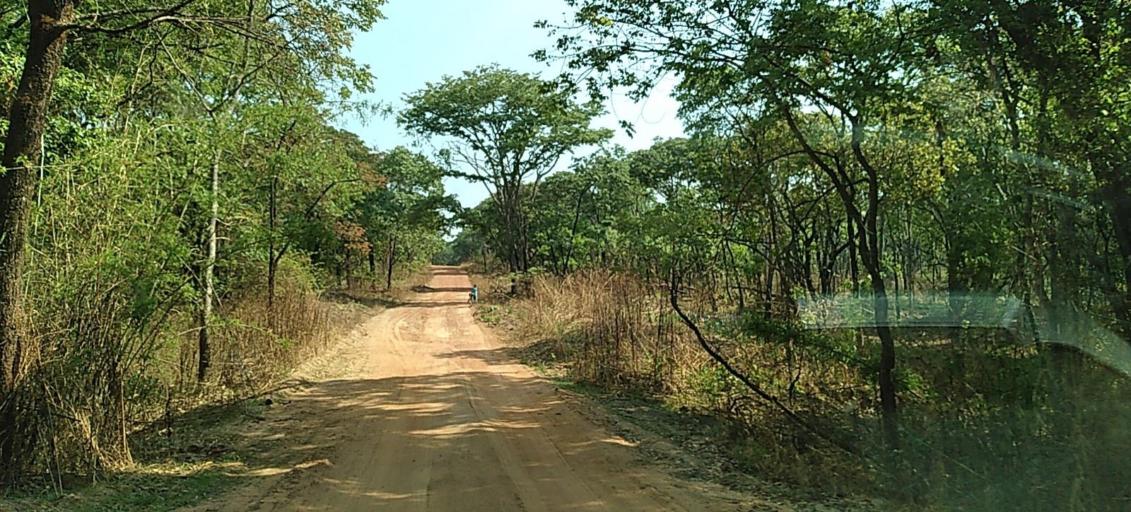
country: ZM
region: Copperbelt
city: Kalulushi
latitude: -12.9346
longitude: 27.8214
